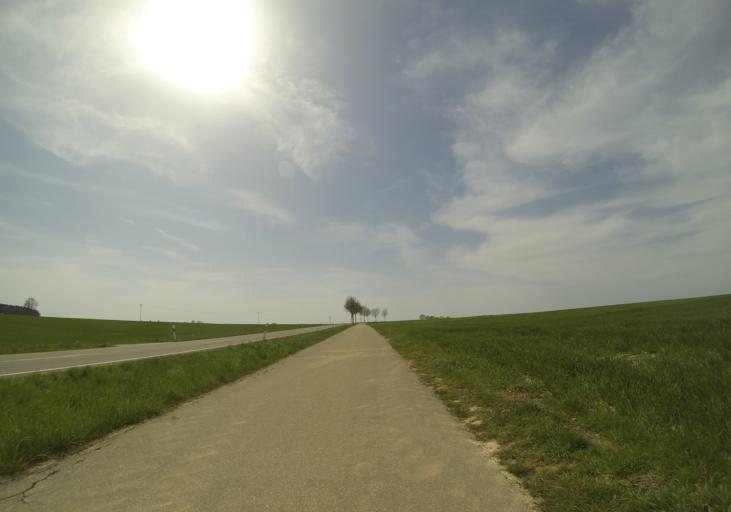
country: DE
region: Baden-Wuerttemberg
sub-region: Tuebingen Region
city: Huttisheim
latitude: 48.2612
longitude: 9.9438
